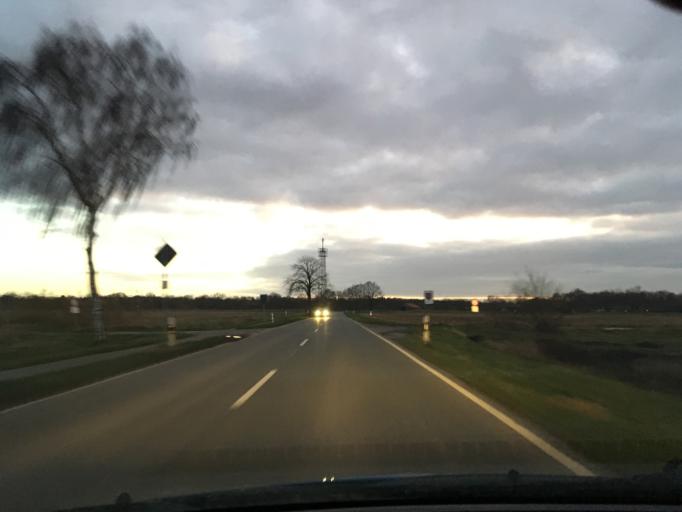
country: DE
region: Lower Saxony
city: Barum
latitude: 53.3606
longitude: 10.4114
